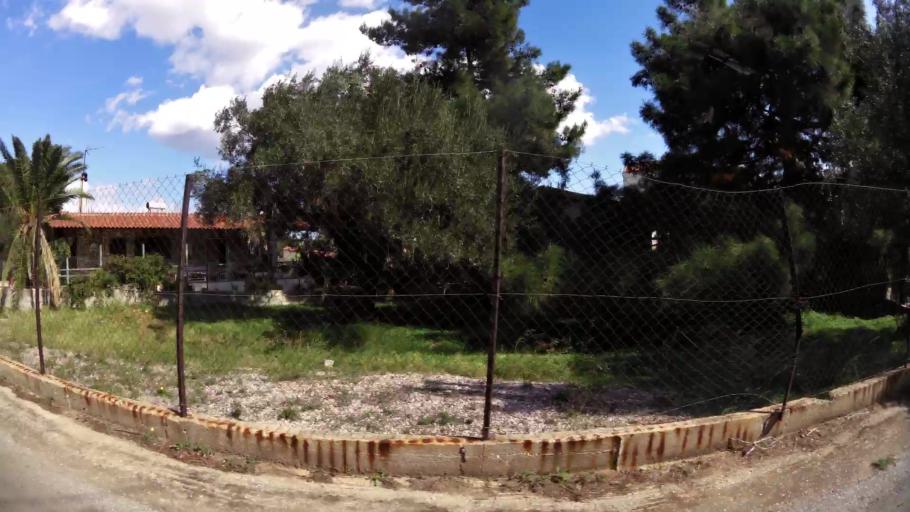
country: GR
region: Attica
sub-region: Nomarchia Anatolikis Attikis
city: Vari
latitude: 37.8377
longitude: 23.8035
